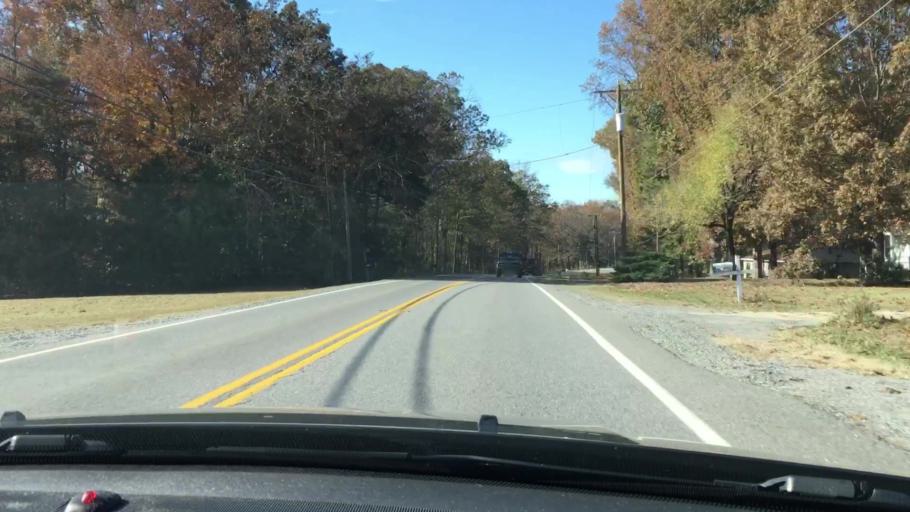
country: US
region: Virginia
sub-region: King William County
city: Central Garage
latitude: 37.7298
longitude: -77.1054
